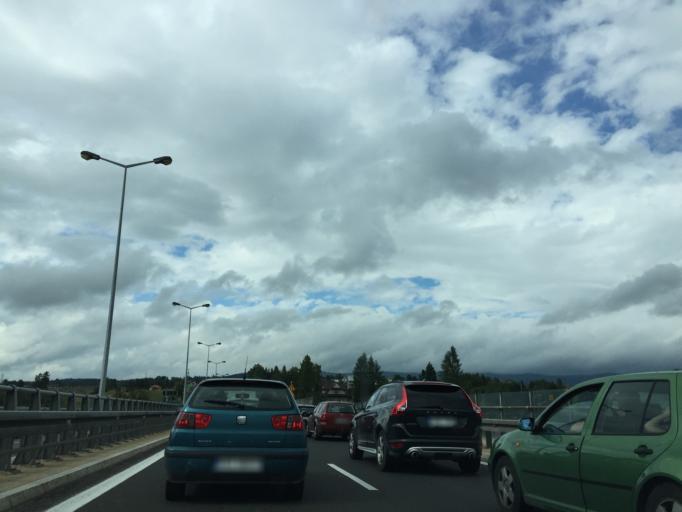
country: PL
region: Lesser Poland Voivodeship
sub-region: Powiat nowotarski
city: Rokiciny
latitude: 49.5960
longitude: 19.9304
